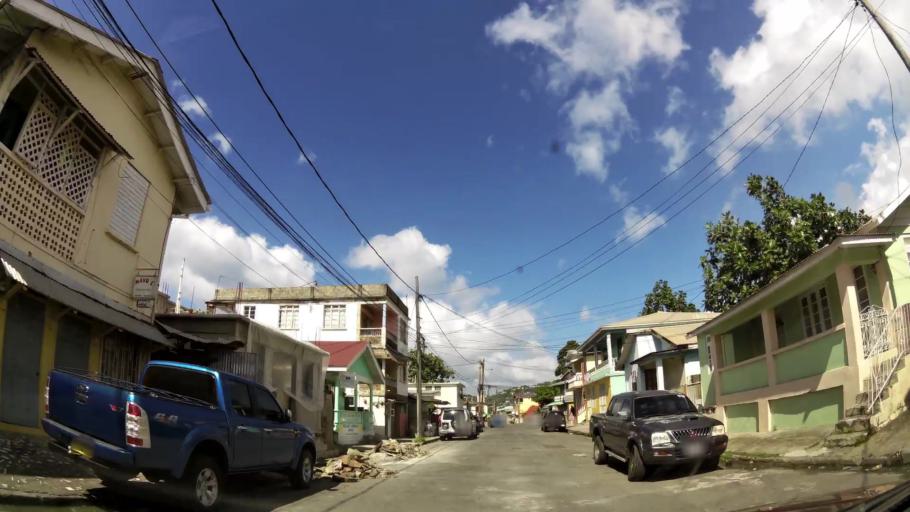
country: DM
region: Saint George
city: Roseau
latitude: 15.3011
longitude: -61.3895
